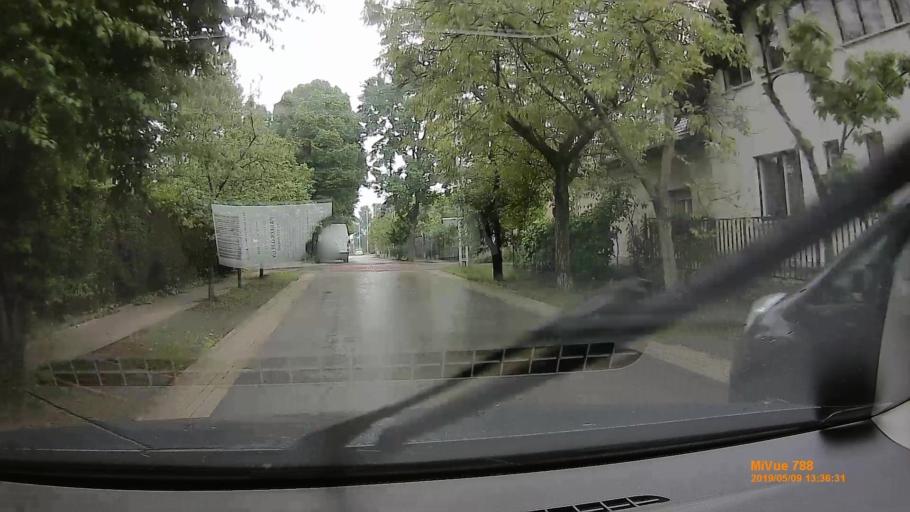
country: HU
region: Budapest
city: Budapest XVI. keruelet
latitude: 47.5300
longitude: 19.2001
